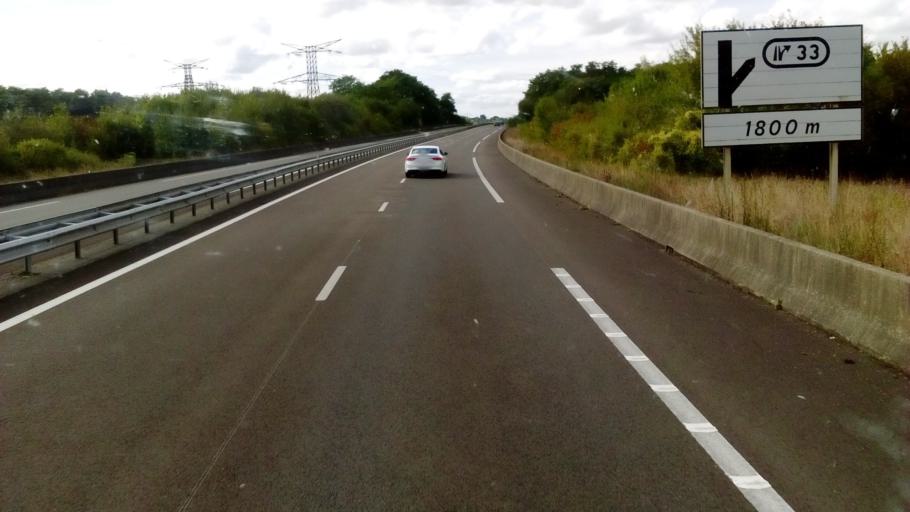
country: FR
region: Bourgogne
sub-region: Departement de la Nievre
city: Coulanges-les-Nevers
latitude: 47.0259
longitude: 3.1717
